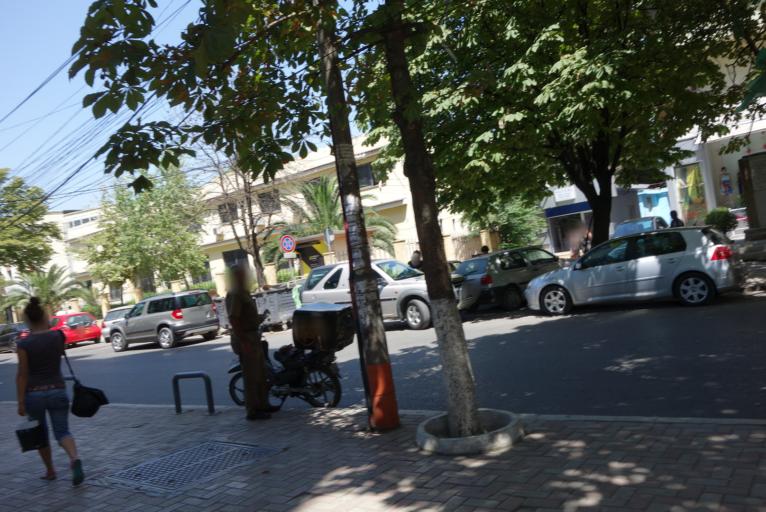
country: AL
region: Tirane
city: Tirana
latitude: 41.3236
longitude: 19.8130
